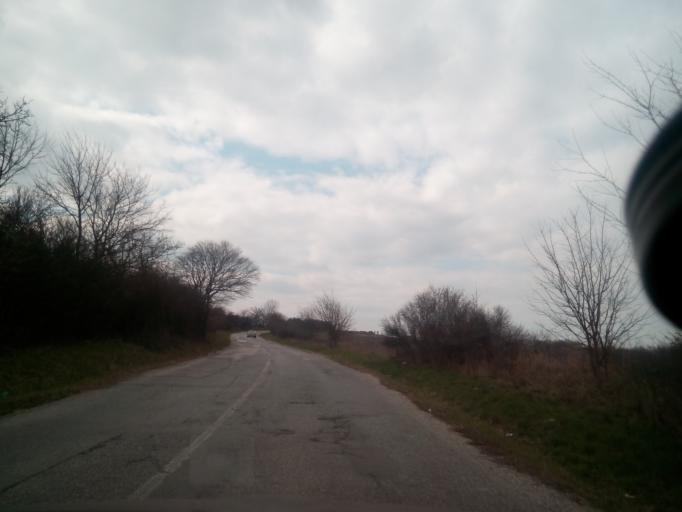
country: SK
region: Kosicky
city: Kosice
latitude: 48.7206
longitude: 21.3003
